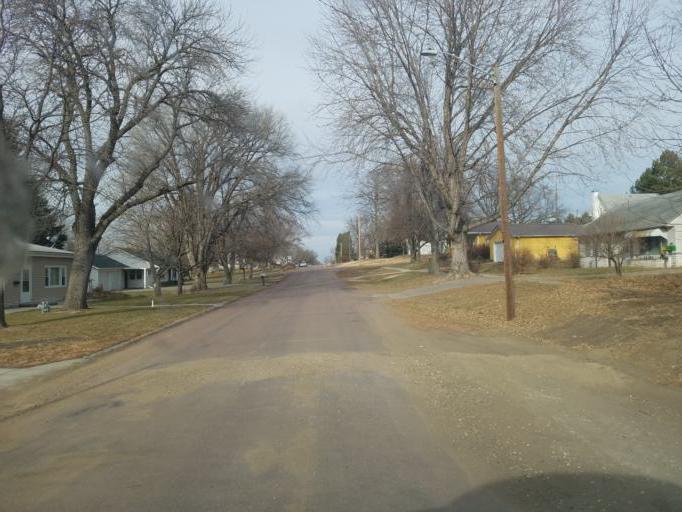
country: US
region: Nebraska
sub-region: Knox County
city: Creighton
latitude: 42.4626
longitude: -97.9091
